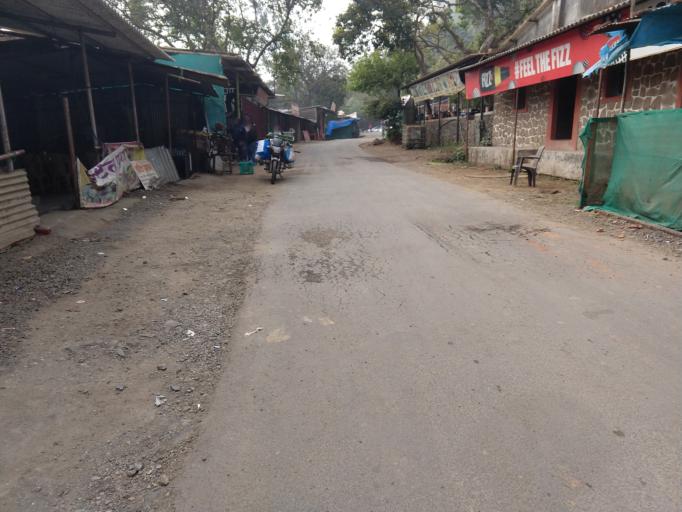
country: IN
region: Maharashtra
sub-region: Pune Division
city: Lonavla
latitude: 18.7091
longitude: 73.4795
